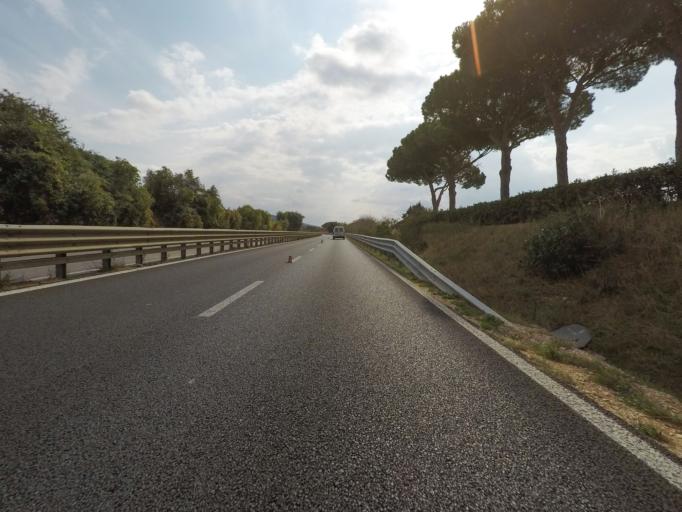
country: IT
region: Tuscany
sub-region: Provincia di Grosseto
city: Grosseto
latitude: 42.7238
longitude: 11.1377
